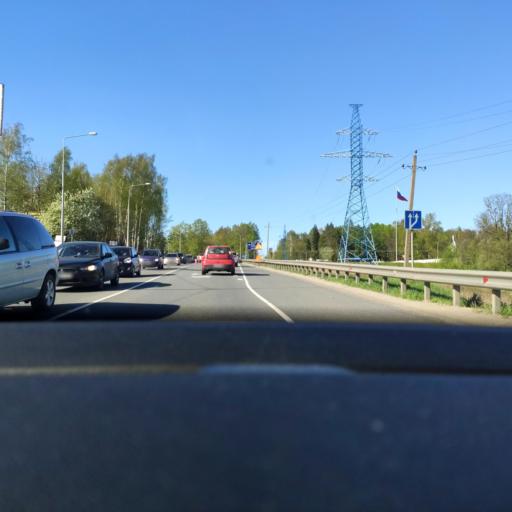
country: RU
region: Moskovskaya
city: Dmitrov
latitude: 56.3560
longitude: 37.4876
